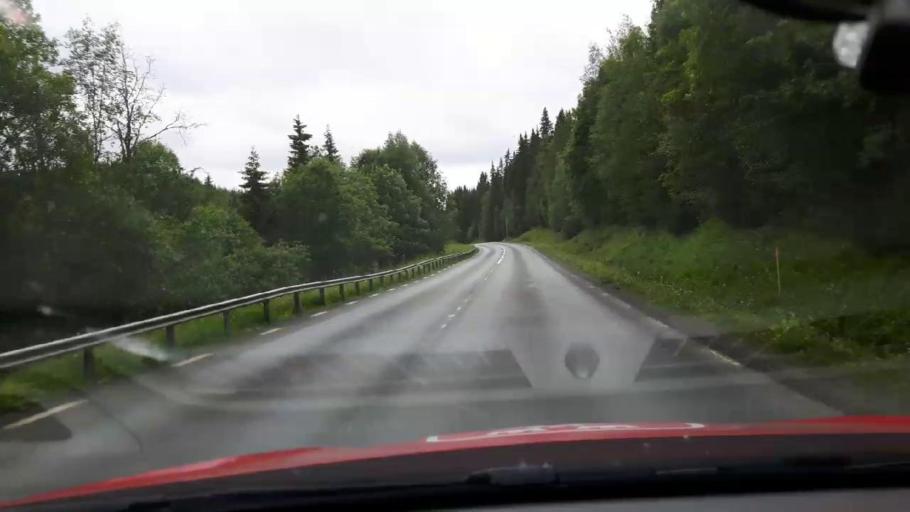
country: SE
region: Jaemtland
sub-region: Are Kommun
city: Are
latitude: 63.3860
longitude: 12.7665
